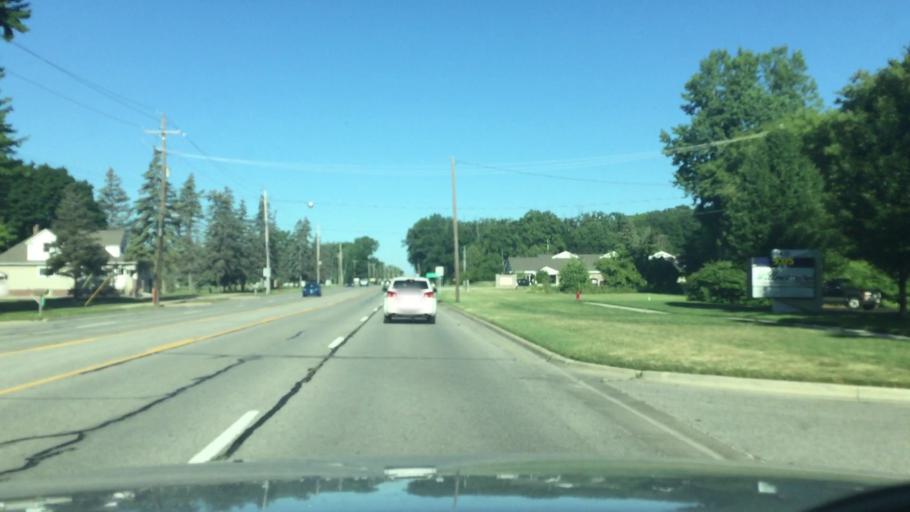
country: US
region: Michigan
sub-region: Saginaw County
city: Shields
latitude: 43.4155
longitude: -84.0302
